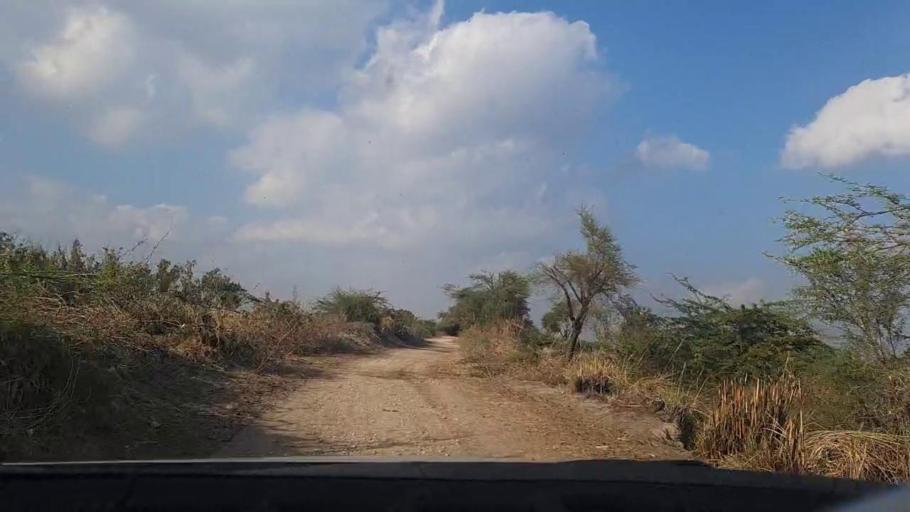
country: PK
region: Sindh
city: Tando Mittha Khan
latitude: 25.9054
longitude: 69.3076
